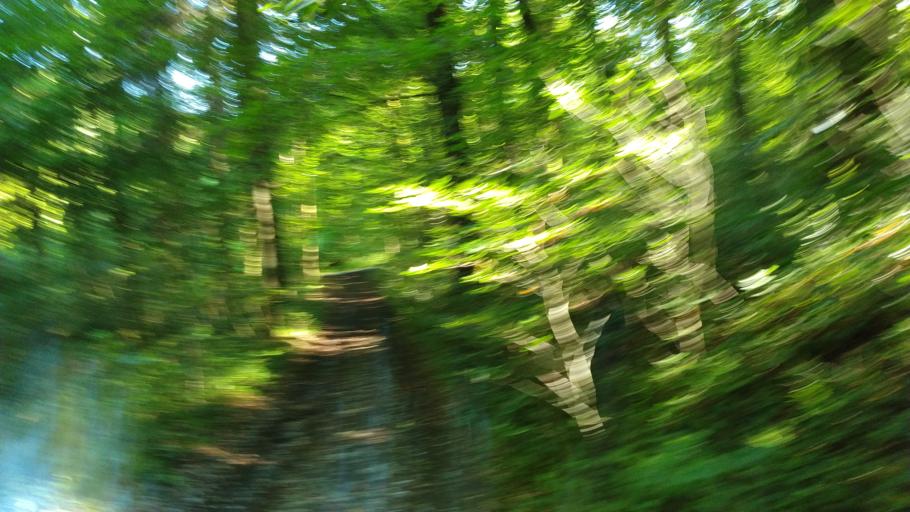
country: BE
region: Wallonia
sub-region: Province du Luxembourg
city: Tellin
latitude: 50.1130
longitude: 5.2084
